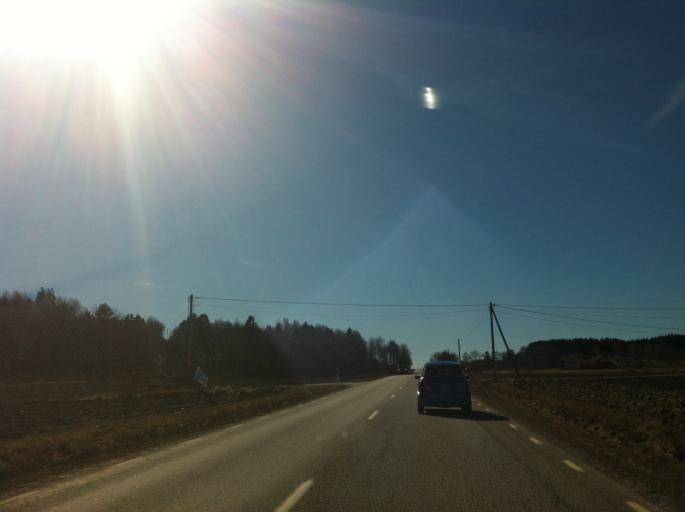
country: SE
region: Vaestra Goetaland
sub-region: Munkedals Kommun
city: Munkedal
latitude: 58.4316
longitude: 11.7146
